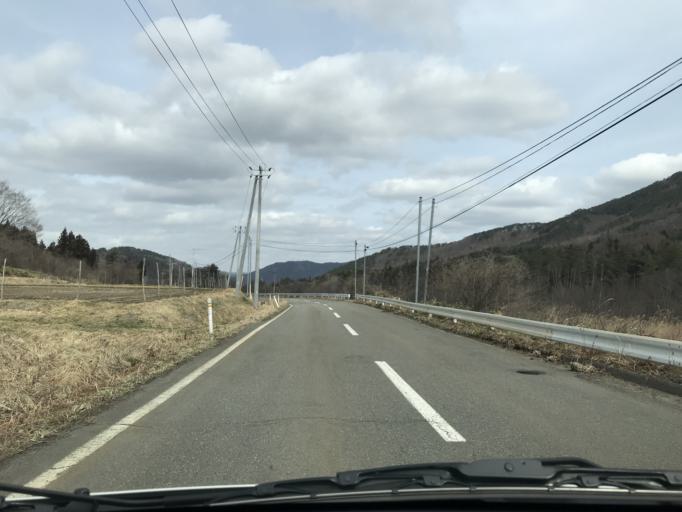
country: JP
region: Iwate
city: Kitakami
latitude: 39.2679
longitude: 141.3212
